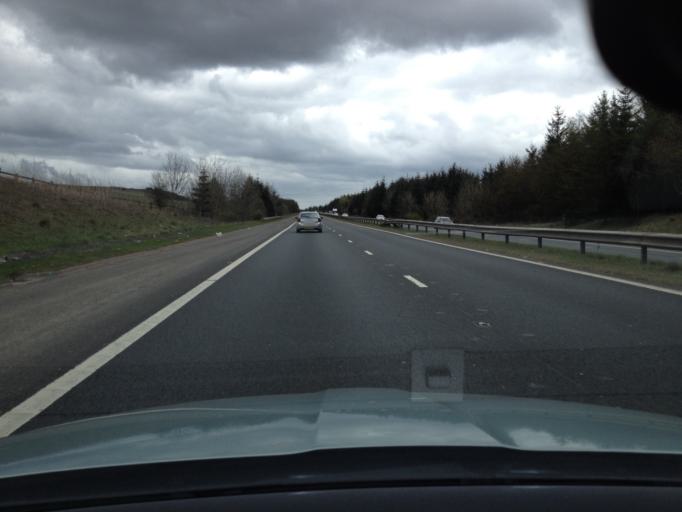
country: GB
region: Scotland
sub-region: North Lanarkshire
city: Caldercruix
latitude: 55.8459
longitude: -3.8724
